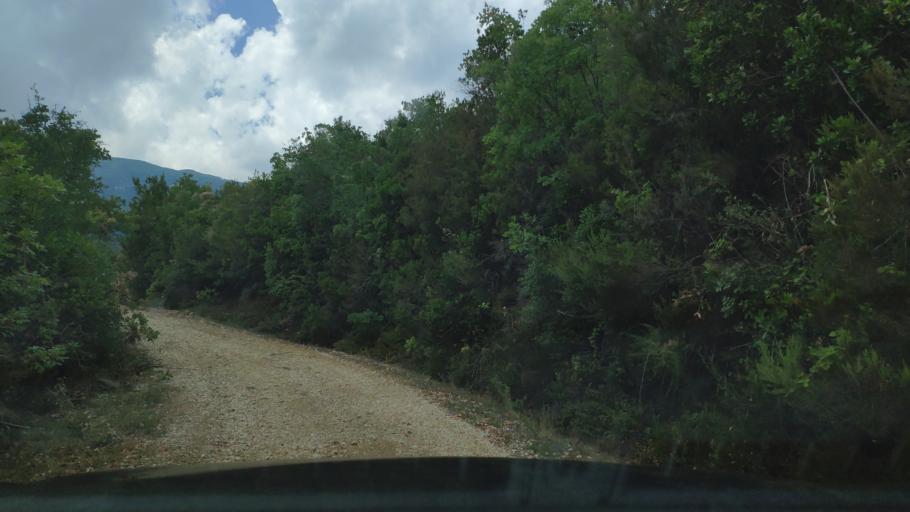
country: GR
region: Epirus
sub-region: Nomos Artas
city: Agios Dimitrios
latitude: 39.3108
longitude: 21.0181
